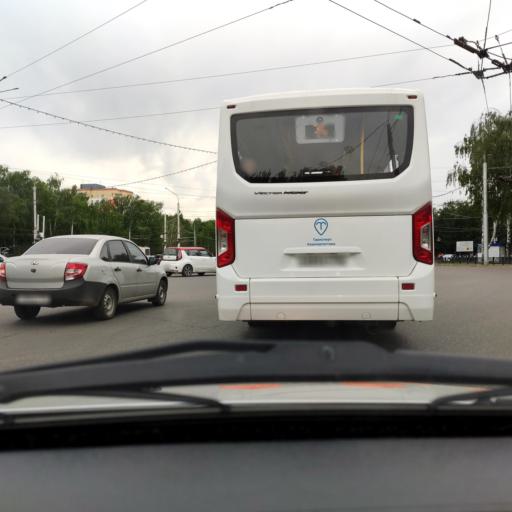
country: RU
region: Bashkortostan
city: Sterlitamak
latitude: 53.6308
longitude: 55.9313
